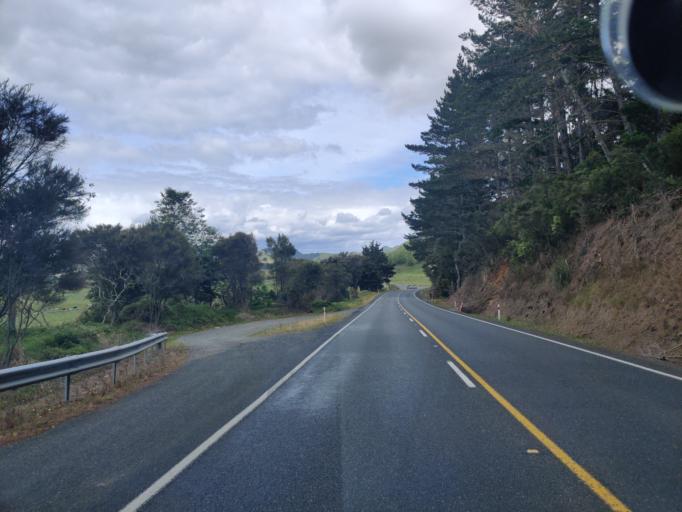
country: NZ
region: Northland
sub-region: Far North District
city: Kerikeri
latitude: -35.0856
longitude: 173.7481
